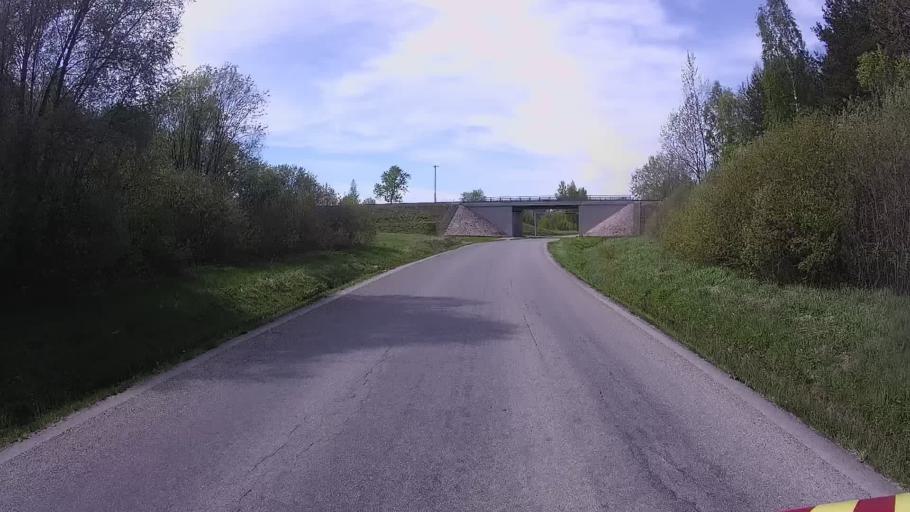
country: EE
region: Valgamaa
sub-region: Valga linn
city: Valga
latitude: 57.7773
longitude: 26.0698
